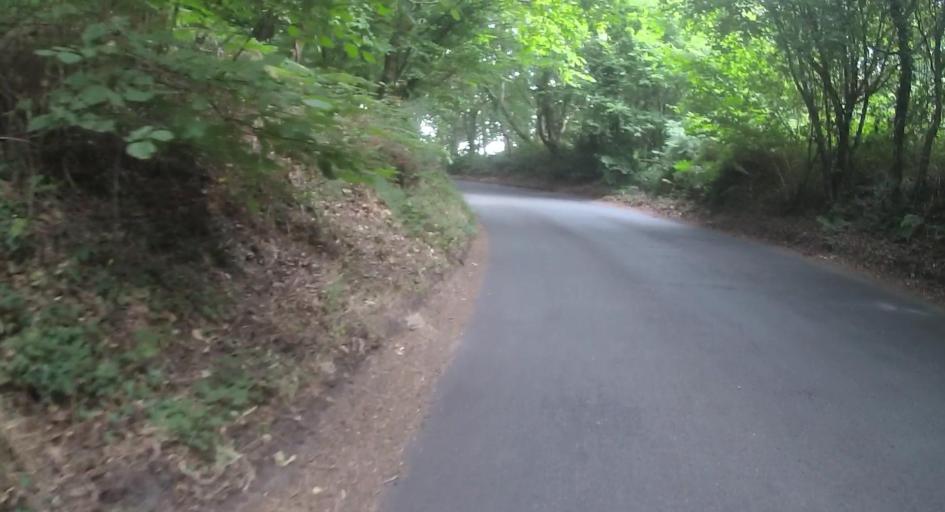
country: GB
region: England
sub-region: Dorset
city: Wool
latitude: 50.6705
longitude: -2.1718
